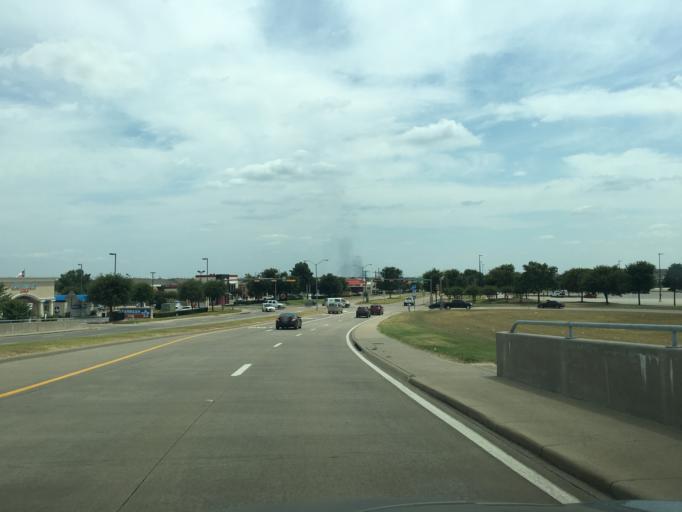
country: US
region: Texas
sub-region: Collin County
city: Frisco
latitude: 33.0992
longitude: -96.7972
